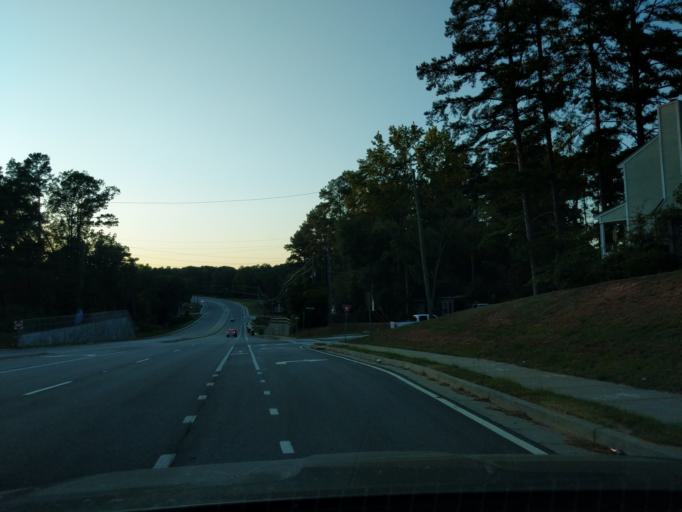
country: US
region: Georgia
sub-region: Columbia County
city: Martinez
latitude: 33.5236
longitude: -82.0906
